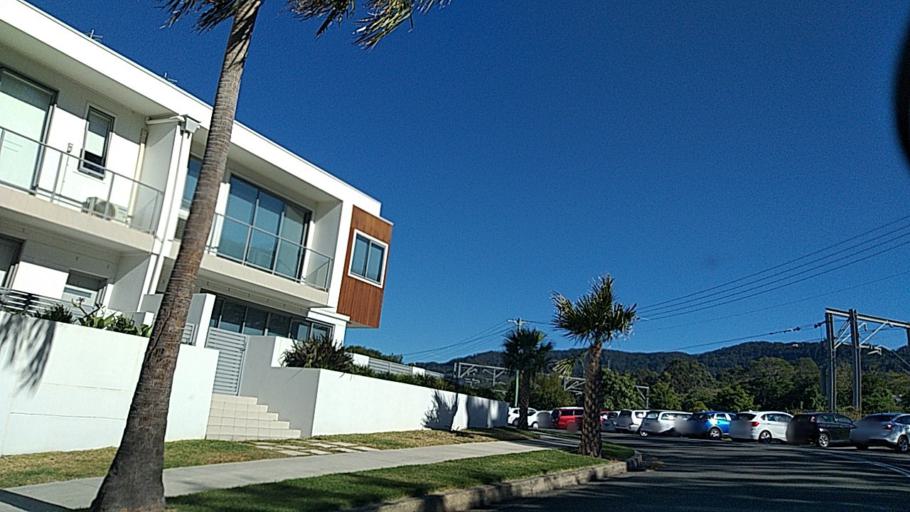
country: AU
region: New South Wales
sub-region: Wollongong
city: Bulli
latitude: -34.3139
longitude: 150.9229
